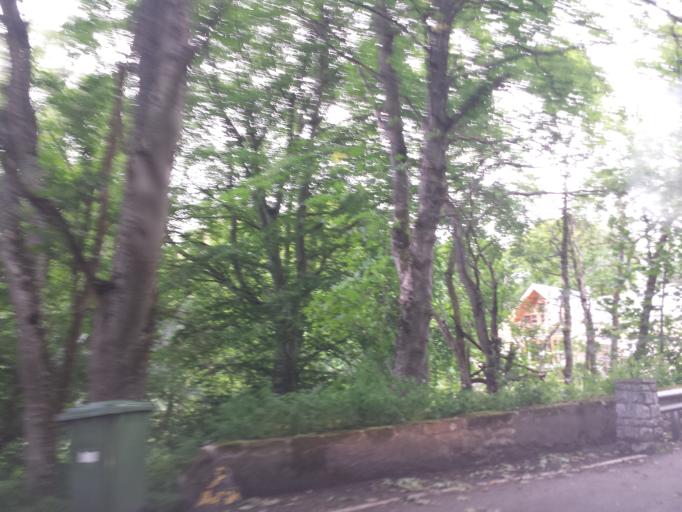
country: GB
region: Scotland
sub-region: Highland
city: Nairn
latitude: 57.5066
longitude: -4.0039
